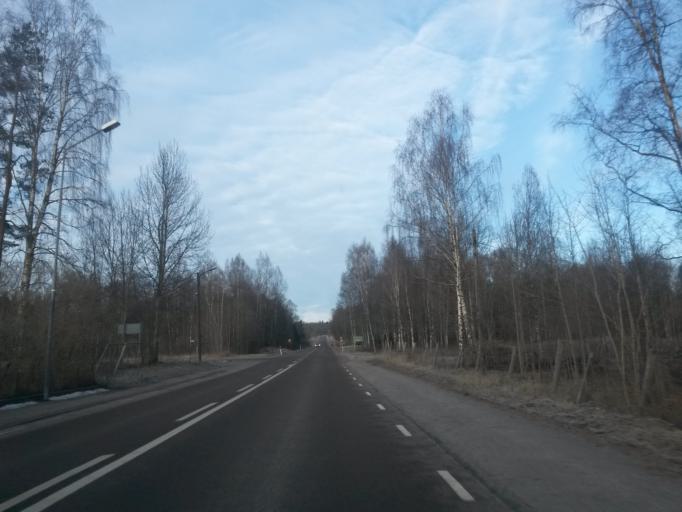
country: SE
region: Vaestra Goetaland
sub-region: Boras Kommun
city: Boras
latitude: 57.8297
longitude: 12.9957
